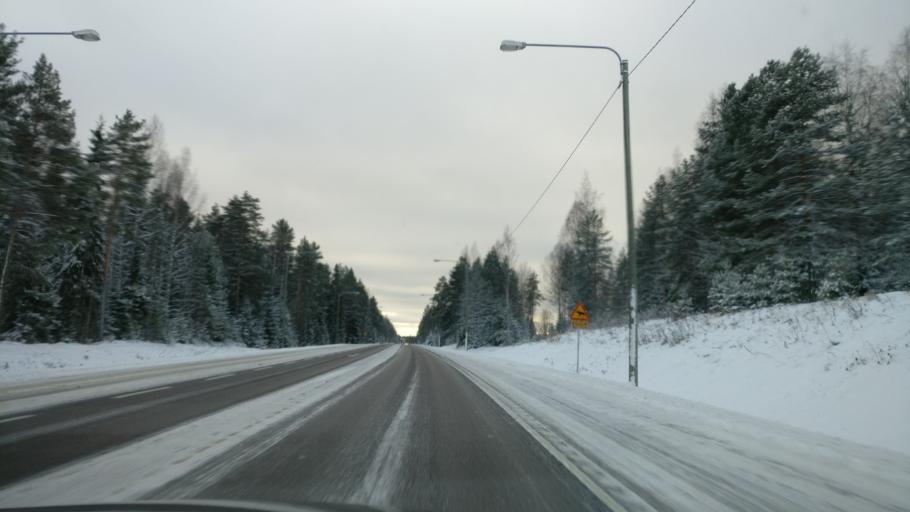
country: FI
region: Paijanne Tavastia
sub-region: Lahti
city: Heinola
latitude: 61.3302
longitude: 26.1618
